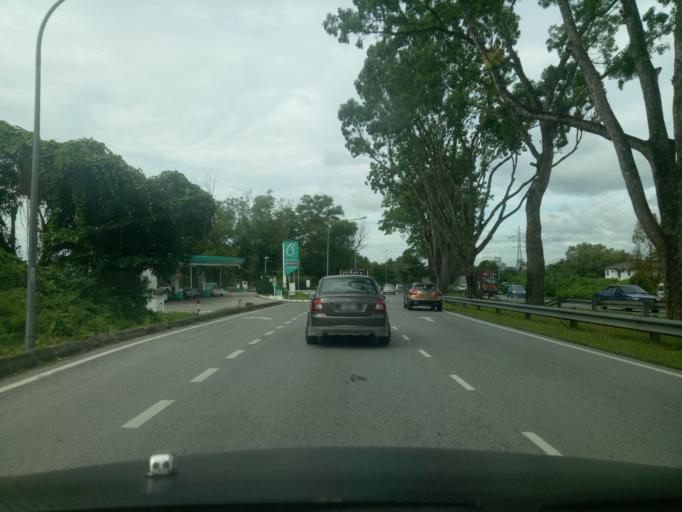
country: MY
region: Sarawak
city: Kuching
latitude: 1.5448
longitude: 110.3743
